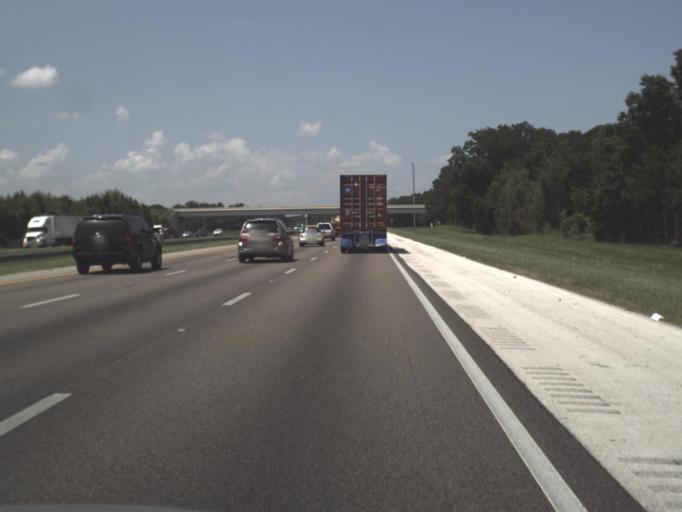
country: US
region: Florida
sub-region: Hillsborough County
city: Dover
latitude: 28.0279
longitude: -82.2123
